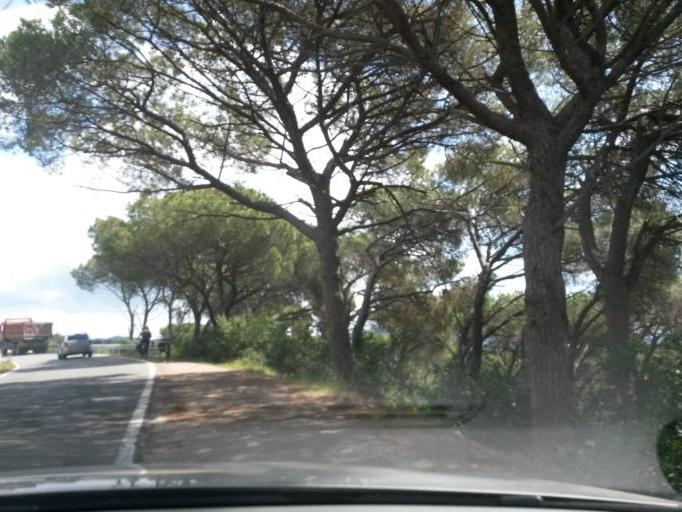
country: IT
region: Tuscany
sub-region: Provincia di Livorno
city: Campo nell'Elba
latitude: 42.7468
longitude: 10.2131
